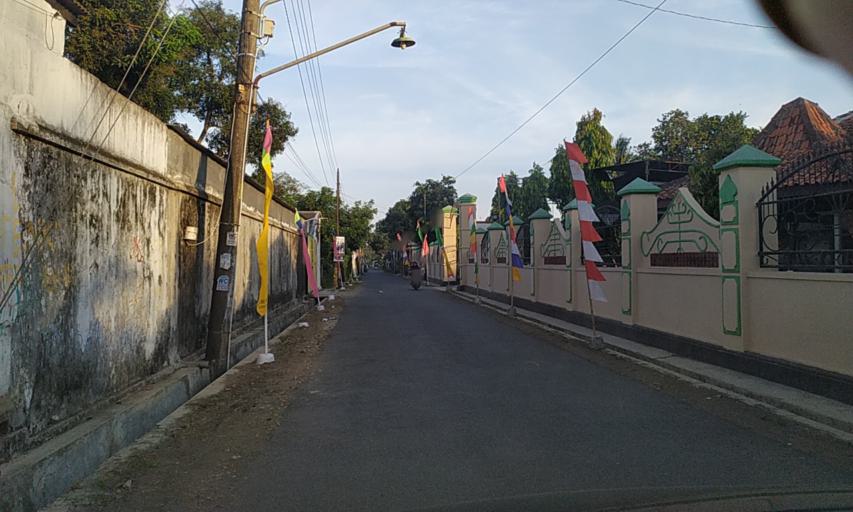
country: ID
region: Central Java
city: Rejanegara
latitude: -7.6893
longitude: 109.0384
